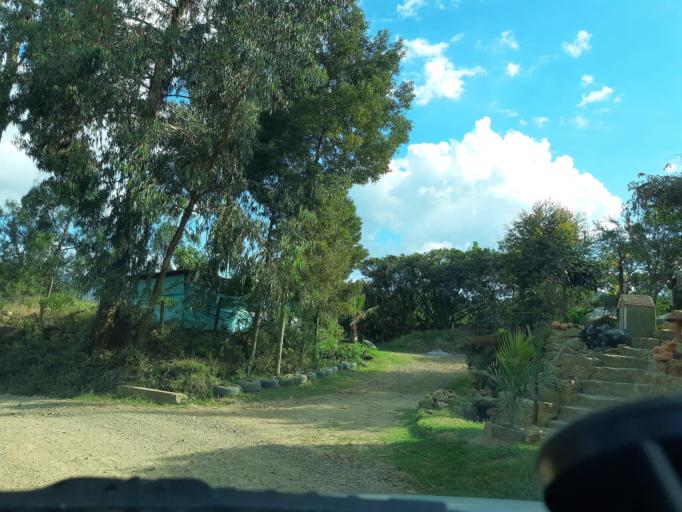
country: CO
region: Boyaca
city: Raquira
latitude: 5.5338
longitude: -73.6474
